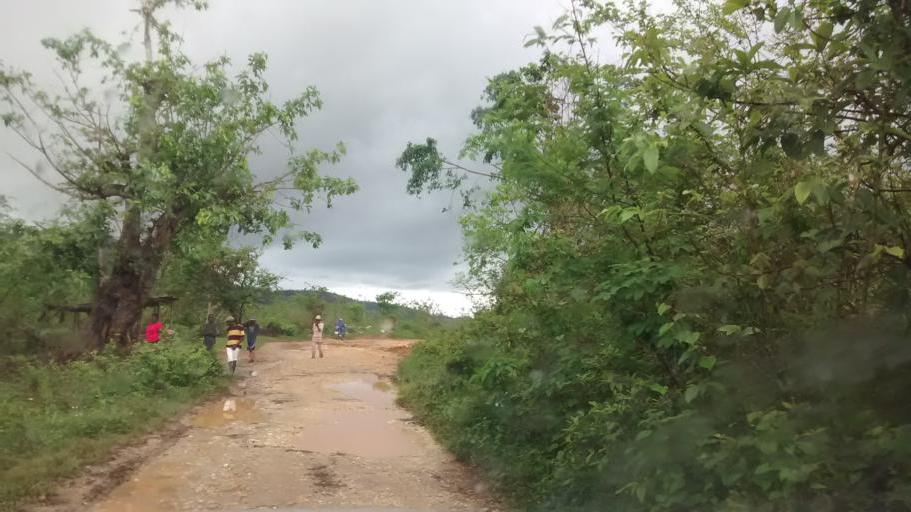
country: HT
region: Grandans
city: Corail
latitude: 18.5381
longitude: -73.9814
